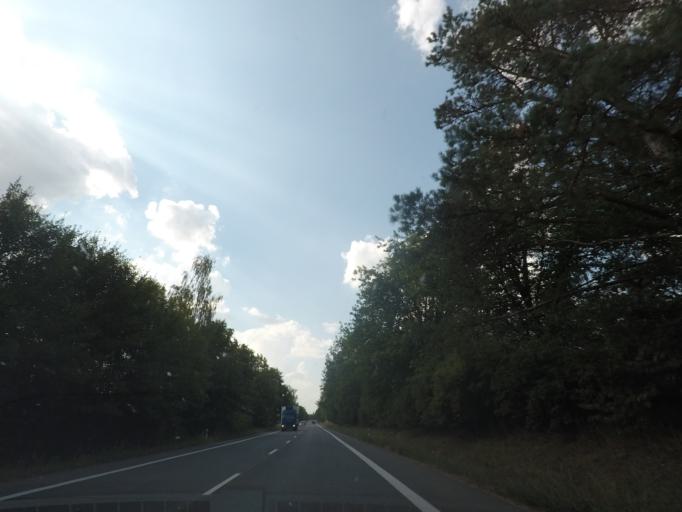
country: CZ
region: Kralovehradecky
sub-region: Okres Nachod
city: Jaromer
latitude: 50.3922
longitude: 15.9049
